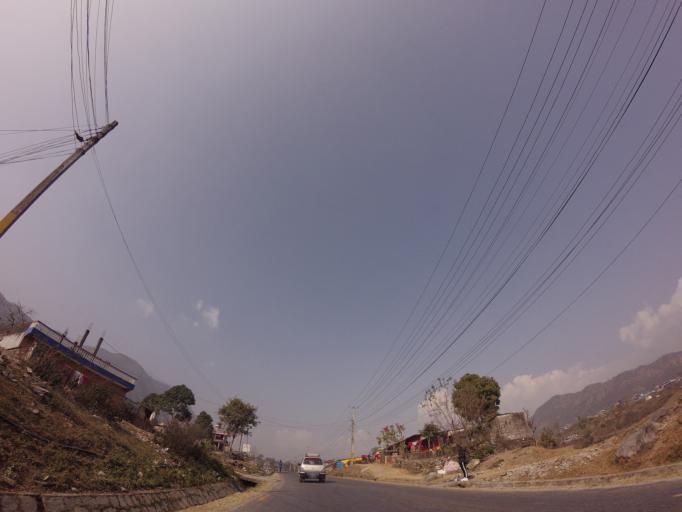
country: NP
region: Western Region
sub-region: Gandaki Zone
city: Pokhara
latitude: 28.2564
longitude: 83.9648
